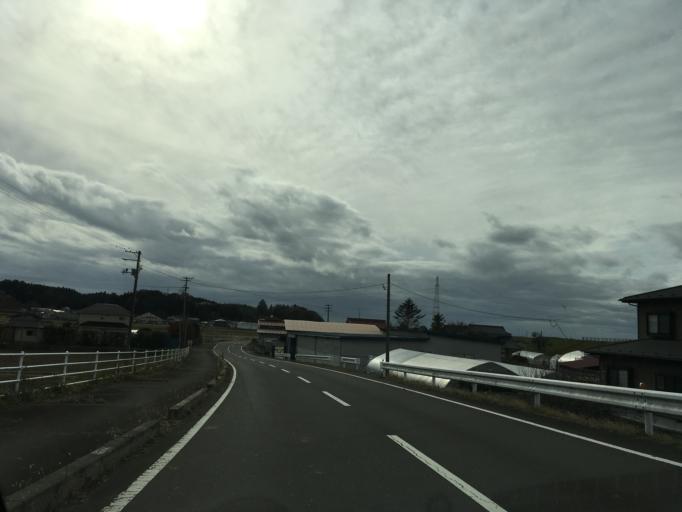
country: JP
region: Iwate
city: Ichinoseki
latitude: 38.7380
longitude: 141.2776
